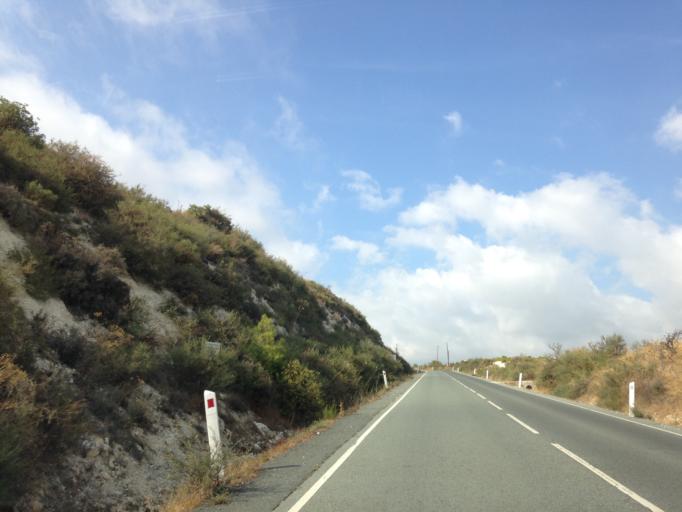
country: CY
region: Limassol
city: Pachna
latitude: 34.8357
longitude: 32.8087
